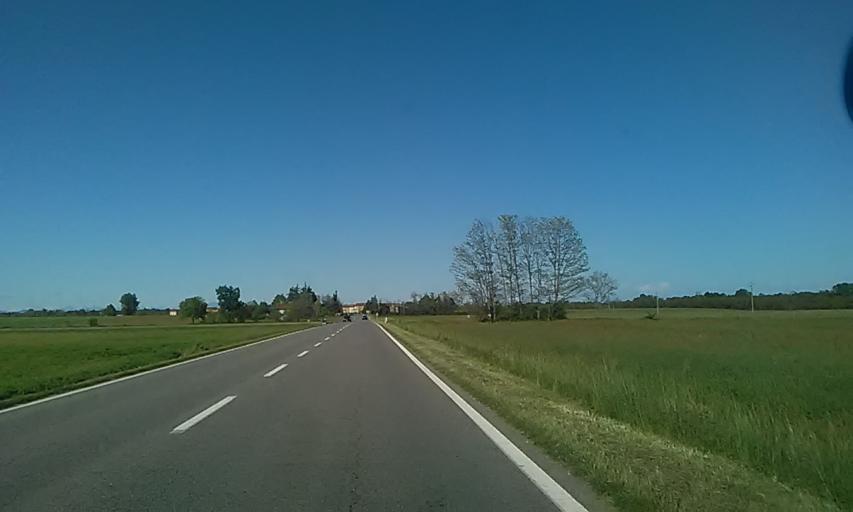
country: IT
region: Piedmont
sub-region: Provincia di Novara
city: Momo
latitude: 45.5810
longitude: 8.5760
